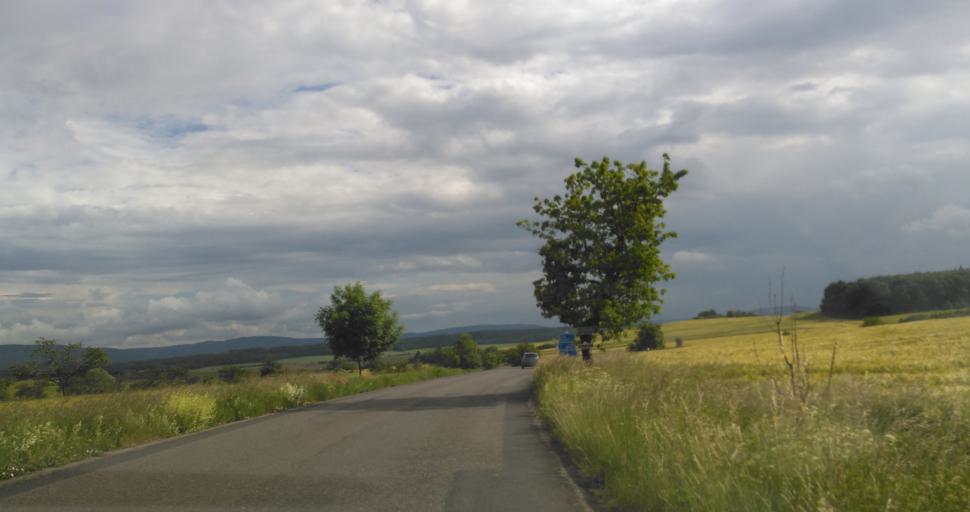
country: CZ
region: Central Bohemia
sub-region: Okres Beroun
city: Beroun
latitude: 49.8971
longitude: 14.0762
